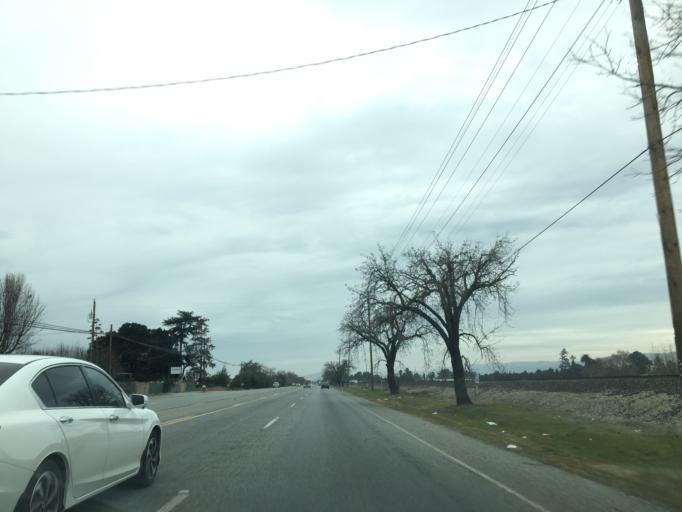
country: US
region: California
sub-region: Santa Clara County
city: San Martin
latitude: 37.0465
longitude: -121.5887
